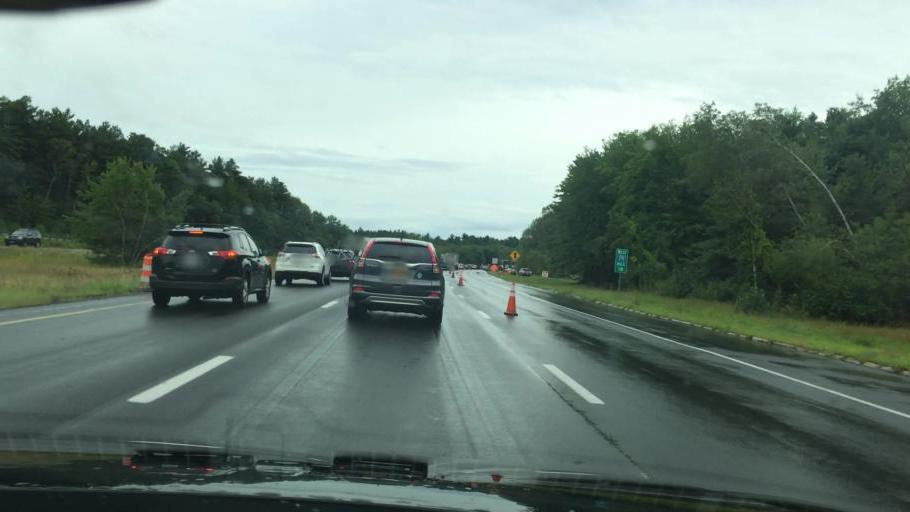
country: US
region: Massachusetts
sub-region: Worcester County
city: Northborough
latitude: 42.3457
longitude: -71.6252
